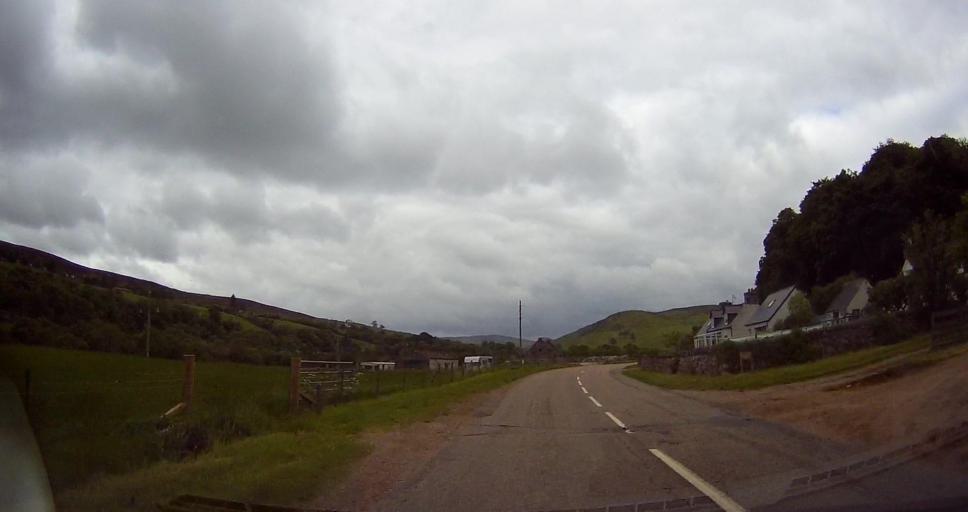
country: GB
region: Scotland
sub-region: Highland
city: Dornoch
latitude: 58.0035
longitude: -4.1984
